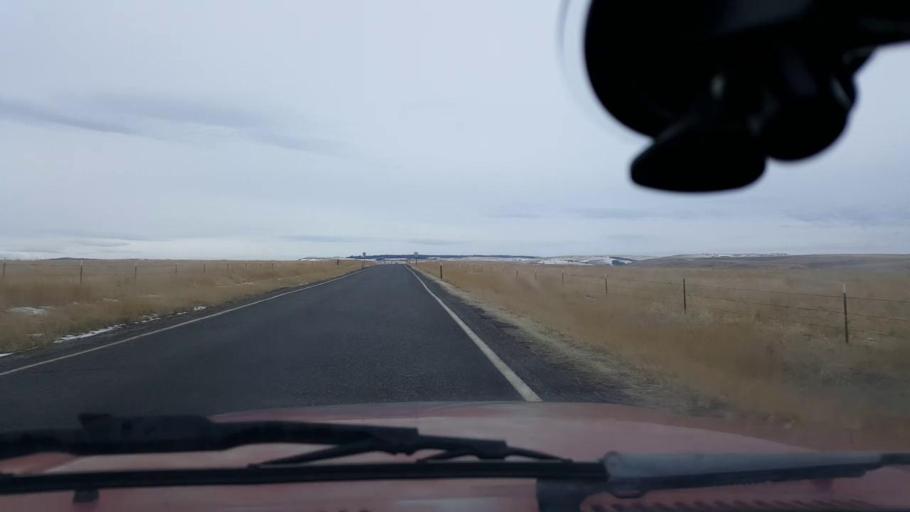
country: US
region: Washington
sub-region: Asotin County
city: Clarkston Heights-Vineland
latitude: 46.3134
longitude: -117.3349
